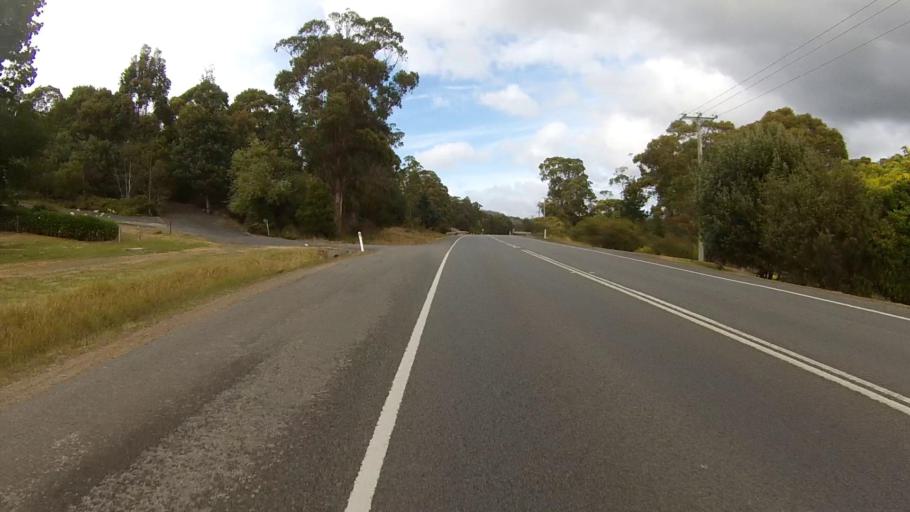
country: AU
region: Tasmania
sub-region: Kingborough
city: Kettering
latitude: -43.0781
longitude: 147.2561
